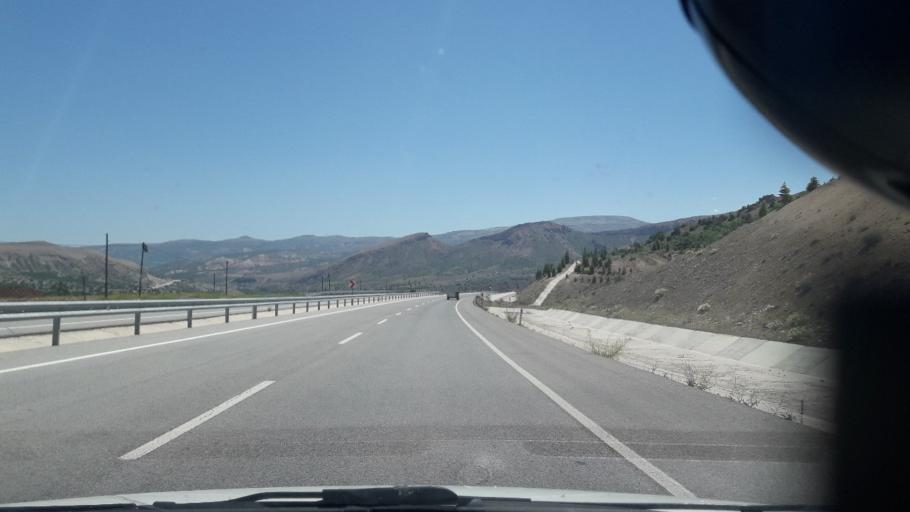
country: TR
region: Malatya
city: Hekimhan
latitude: 38.7915
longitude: 37.9613
